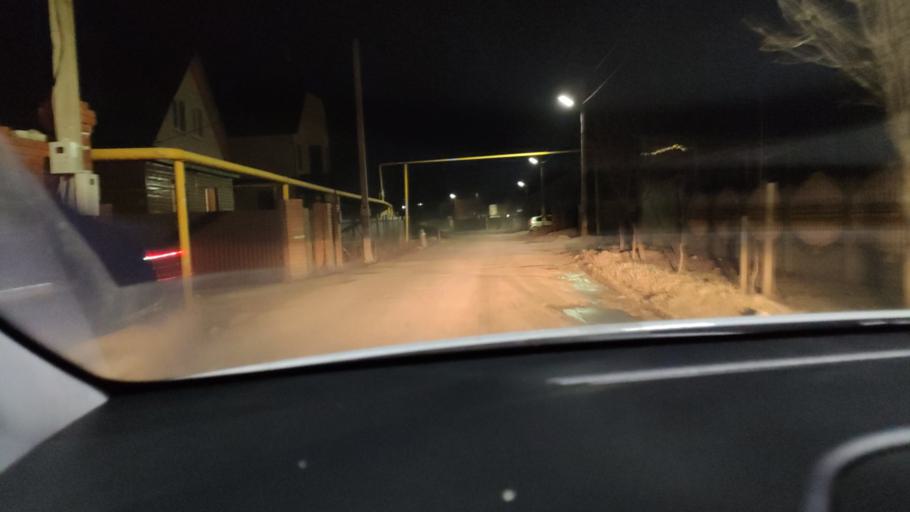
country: RU
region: Tatarstan
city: Stolbishchi
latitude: 55.7633
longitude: 49.2568
